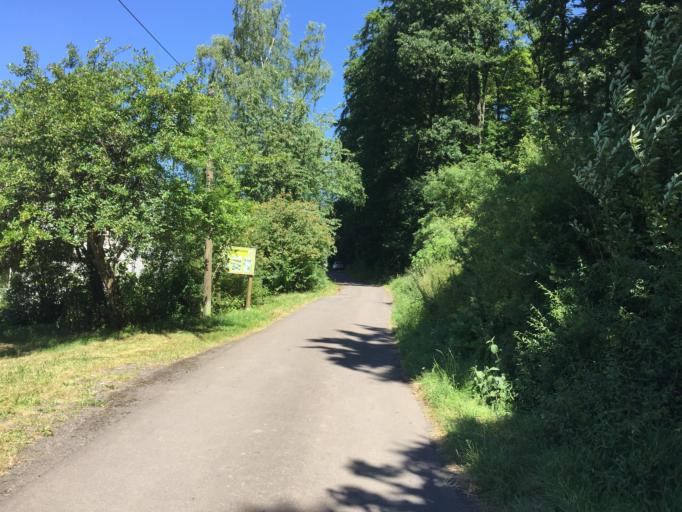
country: DE
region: Hesse
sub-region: Regierungsbezirk Giessen
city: Grossen Buseck
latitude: 50.5975
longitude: 8.8072
